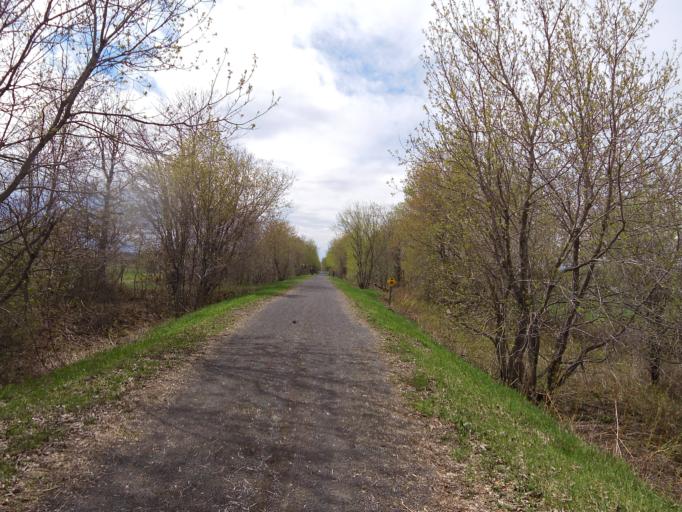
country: CA
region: Ontario
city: Hawkesbury
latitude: 45.5383
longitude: -74.7277
